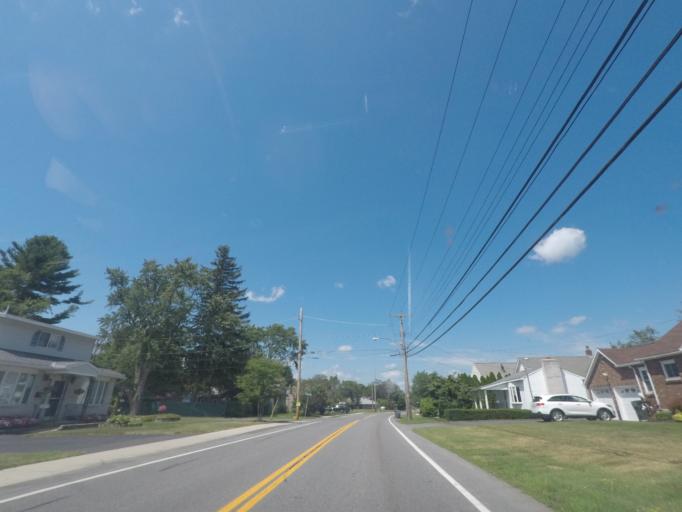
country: US
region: New York
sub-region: Schenectady County
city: Rotterdam
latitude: 42.7742
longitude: -73.9589
